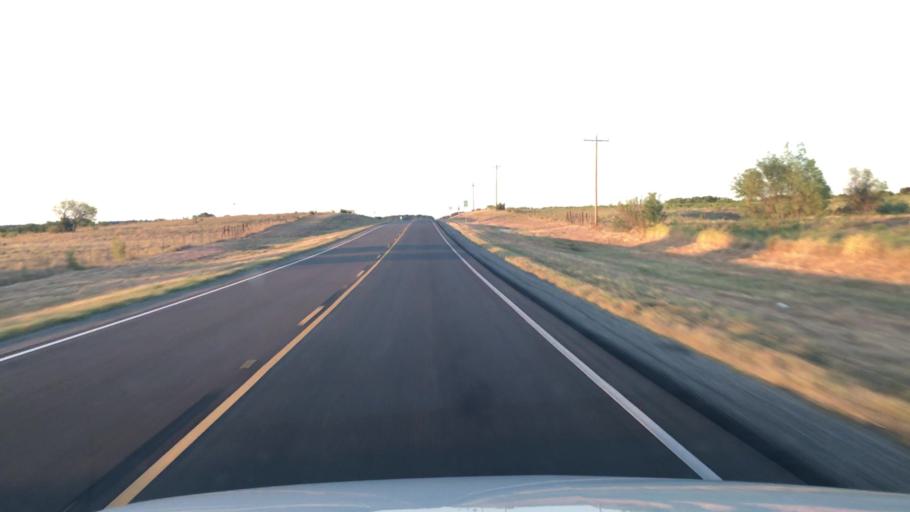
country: US
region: Texas
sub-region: Hamilton County
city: Hico
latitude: 32.0801
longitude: -97.9799
